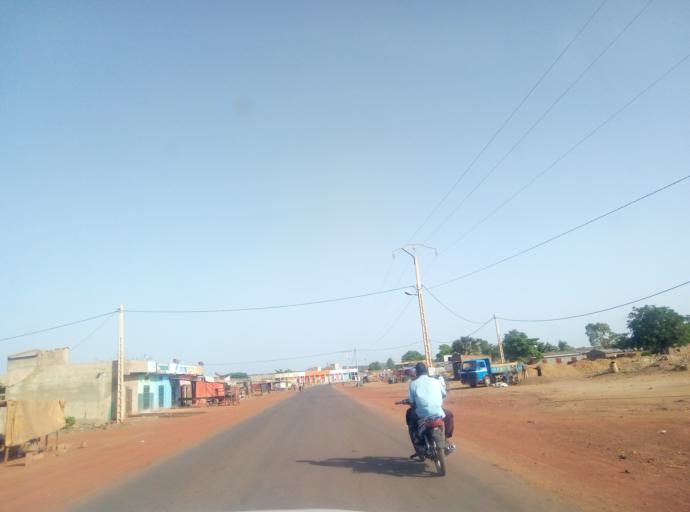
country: ML
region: Bamako
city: Bamako
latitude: 12.5979
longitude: -7.7675
